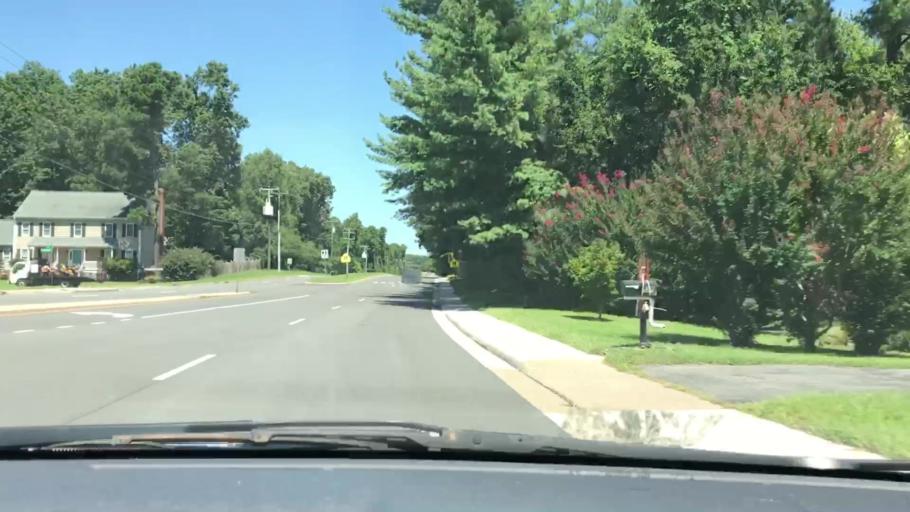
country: US
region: Virginia
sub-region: Henrico County
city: Short Pump
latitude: 37.6137
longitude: -77.6073
